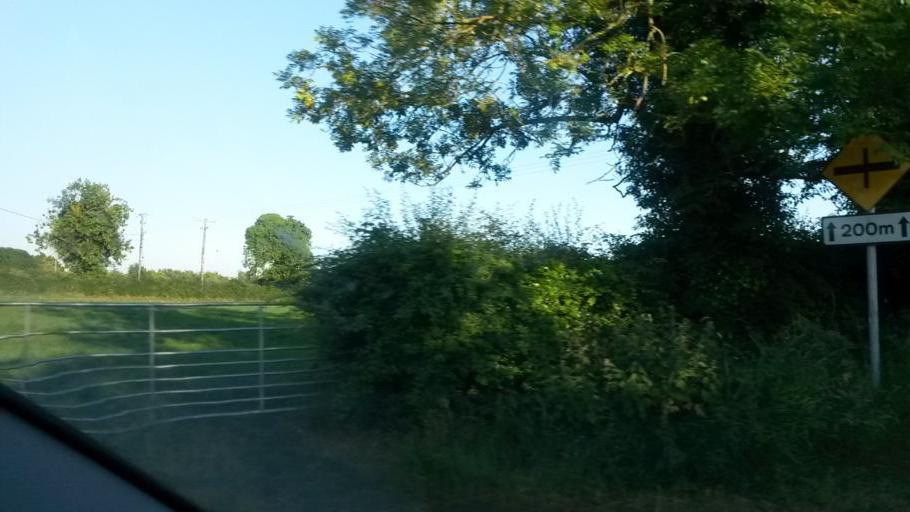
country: IE
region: Leinster
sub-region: An Mhi
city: Ashbourne
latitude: 53.5658
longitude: -6.3528
